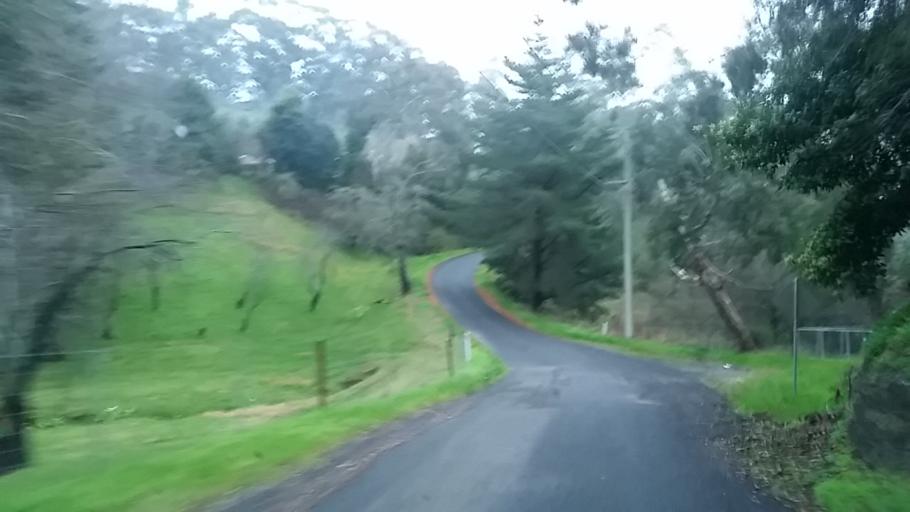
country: AU
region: South Australia
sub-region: Adelaide Hills
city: Adelaide Hills
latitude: -34.9248
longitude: 138.7328
